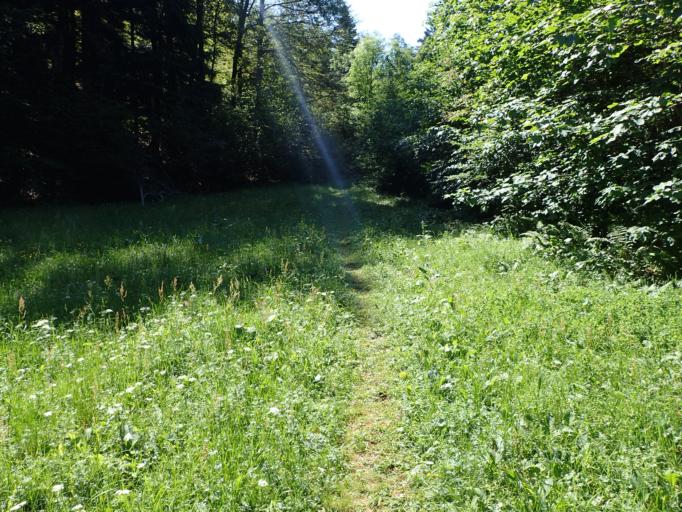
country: AT
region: Salzburg
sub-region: Politischer Bezirk Salzburg-Umgebung
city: Elsbethen
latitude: 47.7509
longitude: 13.1191
